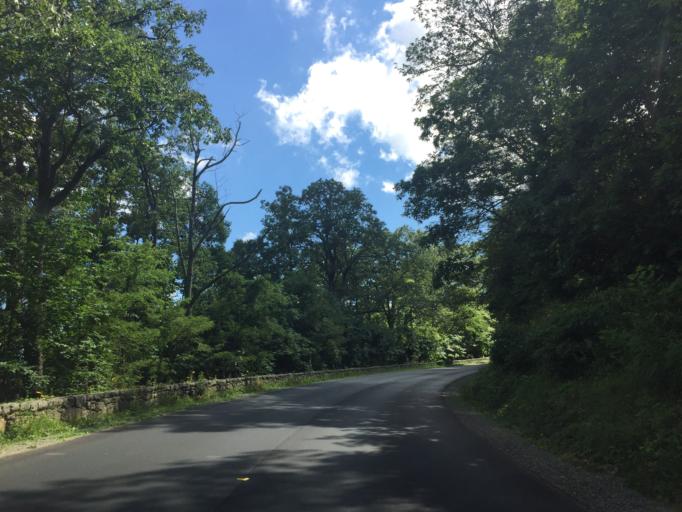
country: US
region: Virginia
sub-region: Page County
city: Luray
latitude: 38.6401
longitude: -78.3127
